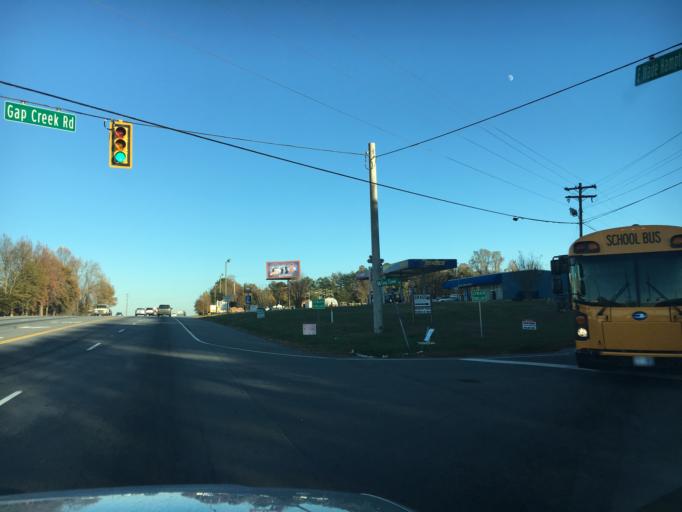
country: US
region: South Carolina
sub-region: Spartanburg County
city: Duncan
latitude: 34.9547
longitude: -82.1697
